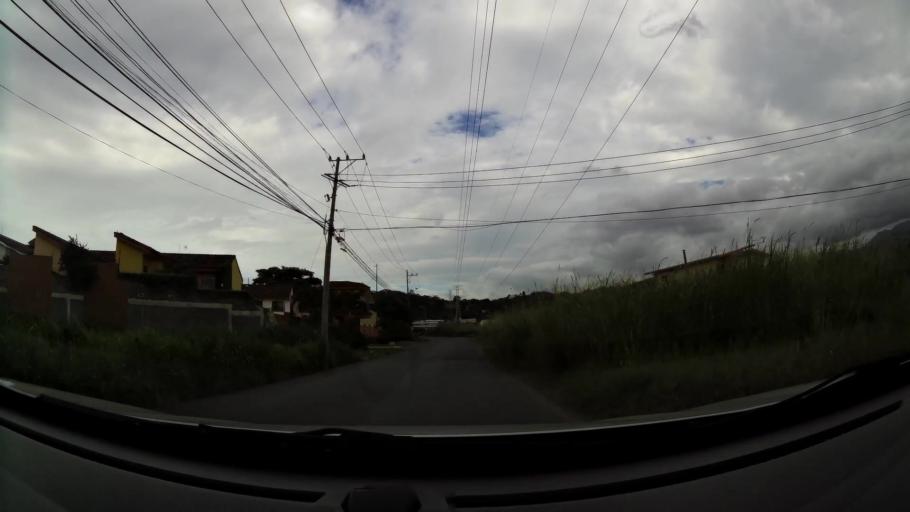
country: CR
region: Heredia
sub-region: Canton de Belen
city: San Antonio
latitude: 9.9661
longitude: -84.1931
